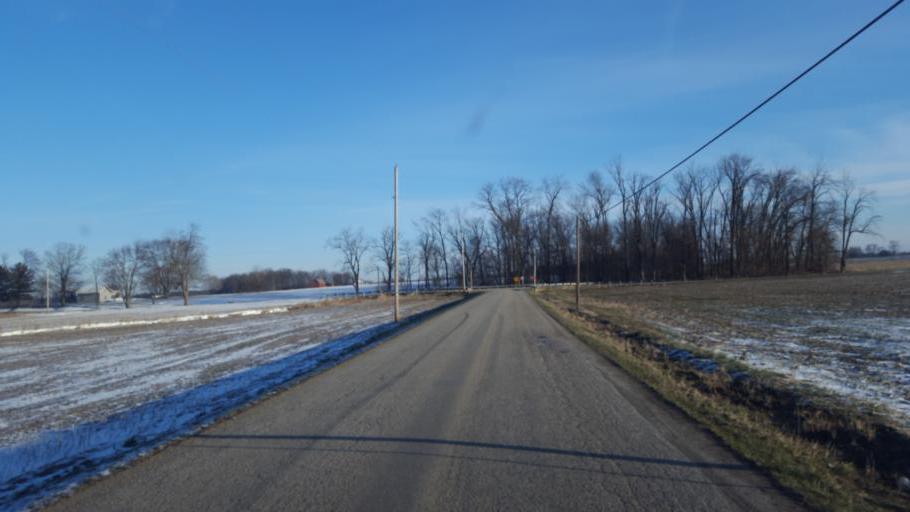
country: US
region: Ohio
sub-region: Morrow County
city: Cardington
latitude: 40.5270
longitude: -82.9053
